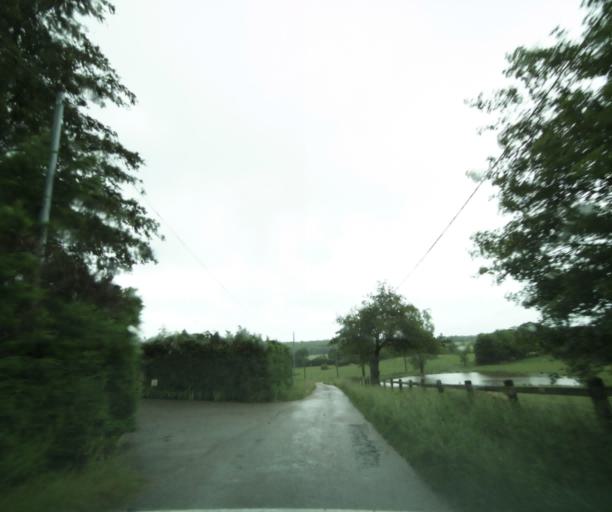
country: FR
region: Bourgogne
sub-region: Departement de Saone-et-Loire
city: Charolles
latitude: 46.4907
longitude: 4.2832
